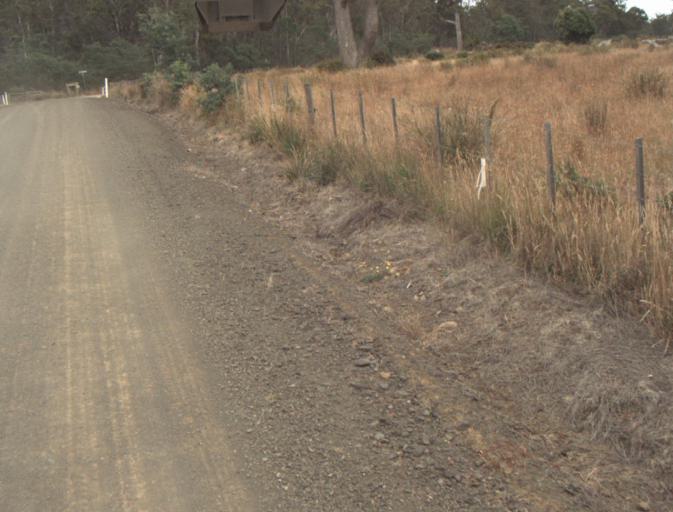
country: AU
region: Tasmania
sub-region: Northern Midlands
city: Evandale
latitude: -41.5199
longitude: 147.3807
